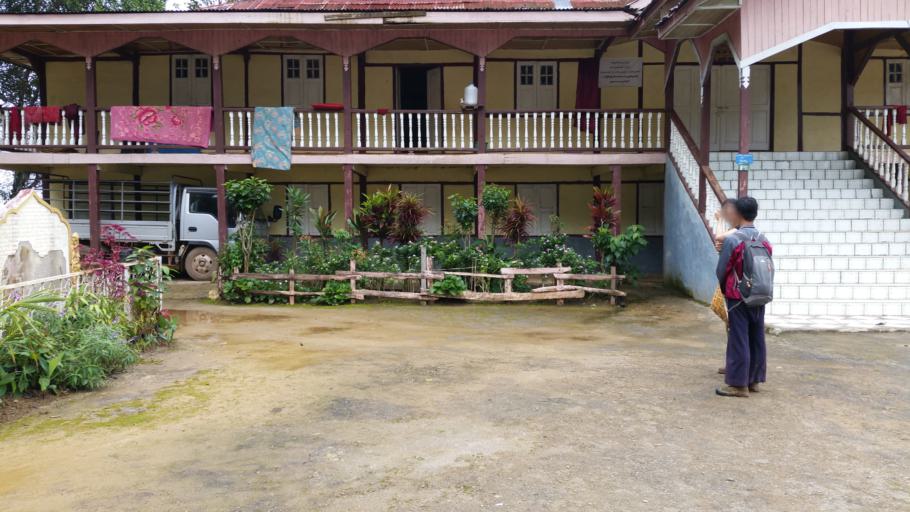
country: MM
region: Mandalay
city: Yamethin
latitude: 20.6176
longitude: 96.5093
